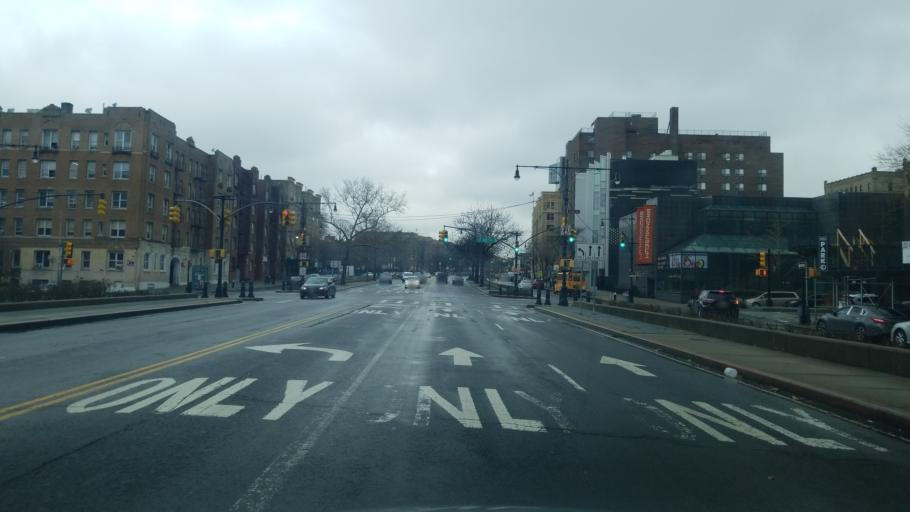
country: US
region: New York
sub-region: New York County
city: Inwood
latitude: 40.8303
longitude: -73.9208
